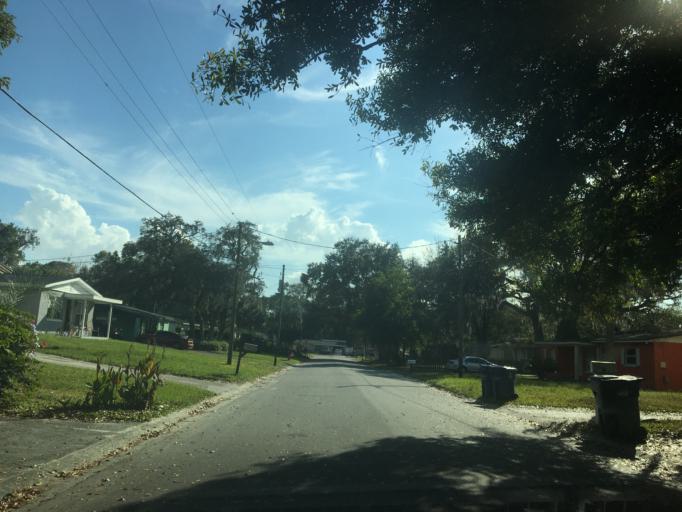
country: US
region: Florida
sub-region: Hillsborough County
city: University
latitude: 28.0411
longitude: -82.4330
